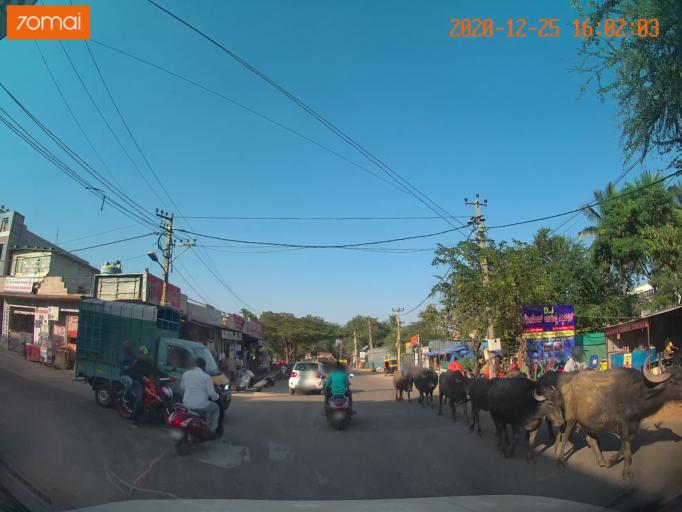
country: IN
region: Karnataka
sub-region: Bangalore Urban
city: Bangalore
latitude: 12.8808
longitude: 77.6246
